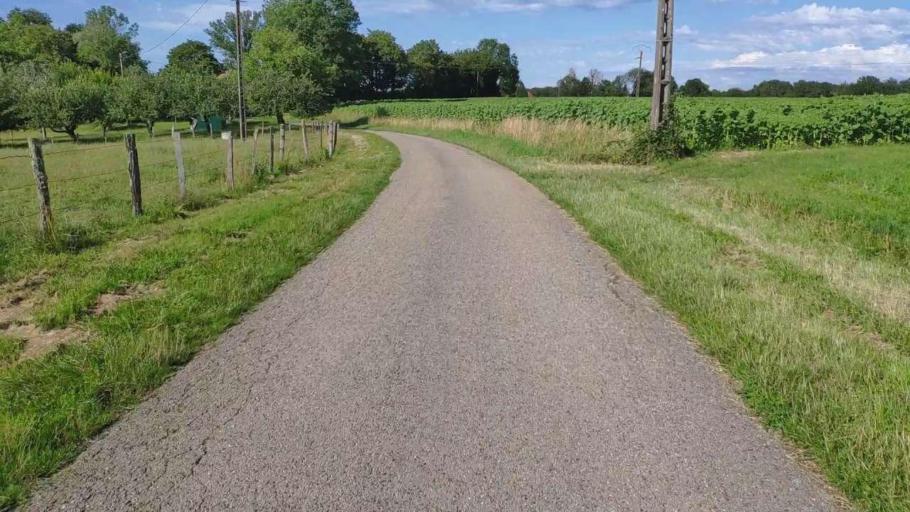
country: FR
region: Franche-Comte
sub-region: Departement du Jura
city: Bletterans
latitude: 46.8213
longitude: 5.4994
